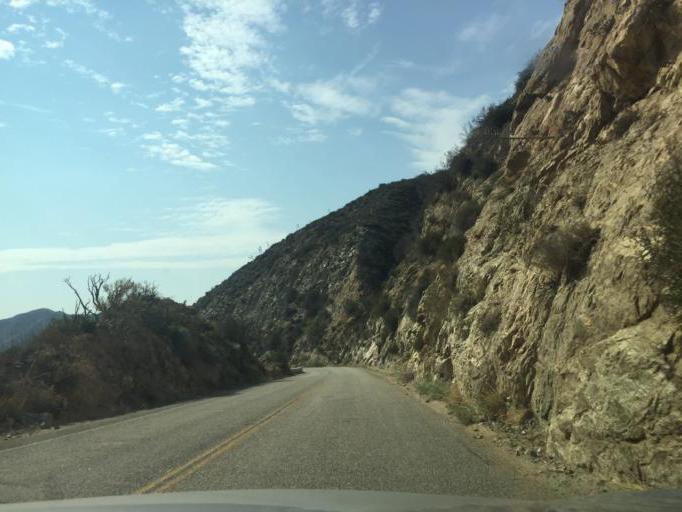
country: US
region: California
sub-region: Los Angeles County
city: Altadena
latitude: 34.2656
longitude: -118.1297
